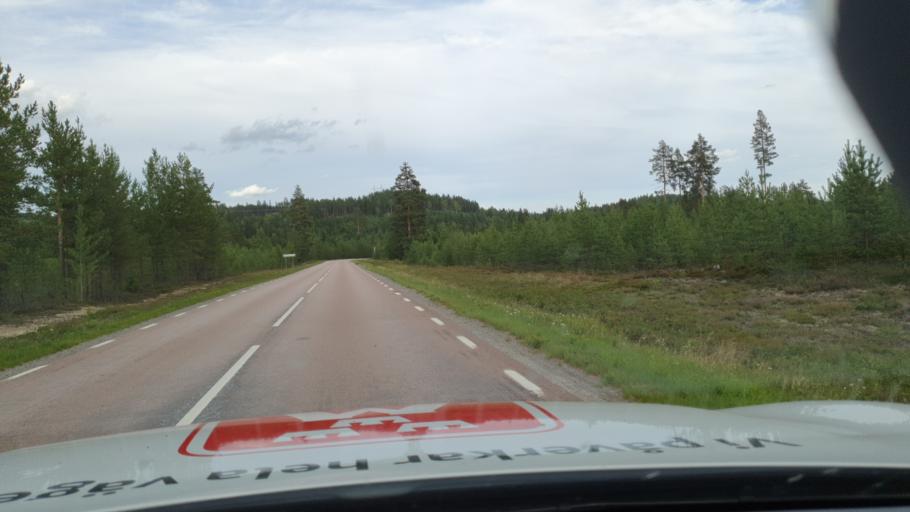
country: SE
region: Vaesternorrland
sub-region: Solleftea Kommun
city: As
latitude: 63.5801
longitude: 16.3808
